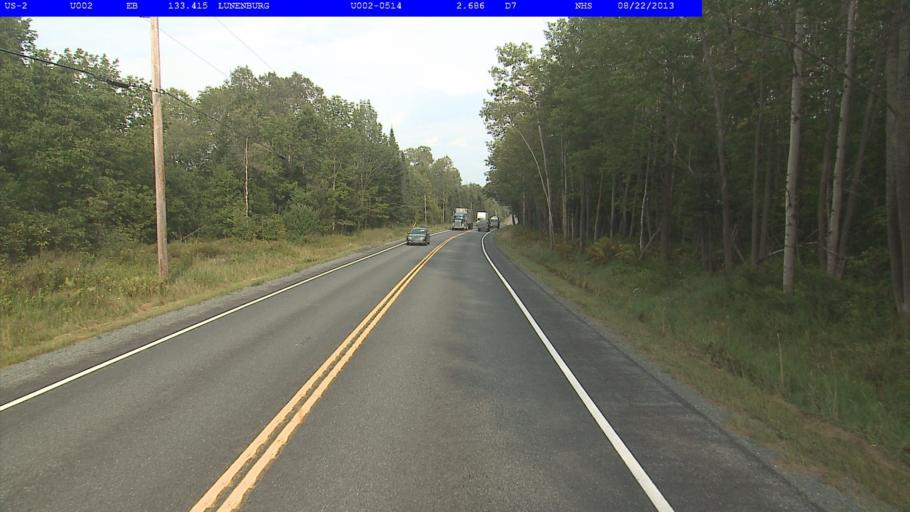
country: US
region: New Hampshire
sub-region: Coos County
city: Whitefield
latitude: 44.4645
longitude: -71.7219
